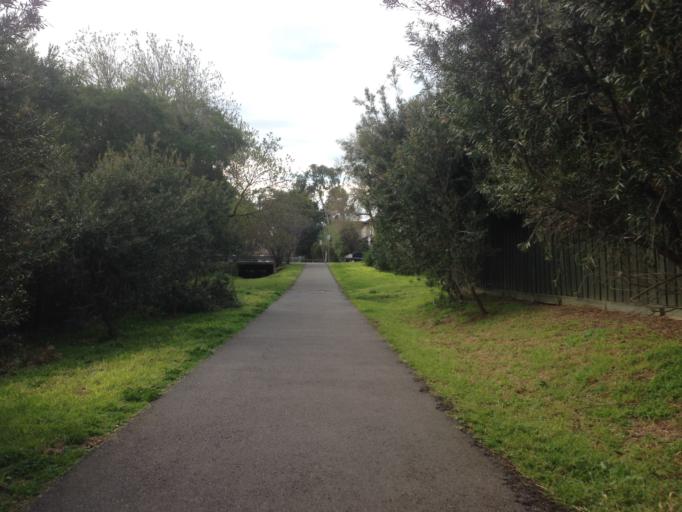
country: AU
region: Victoria
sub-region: Banyule
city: Bellfield
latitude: -37.7659
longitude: 145.0390
